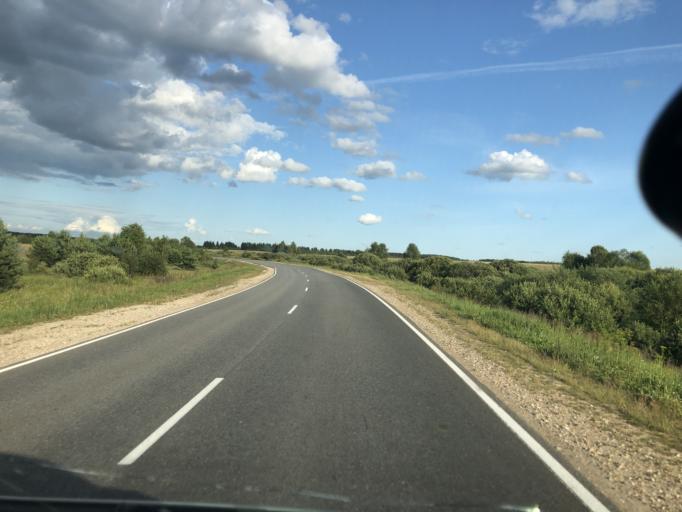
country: RU
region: Kaluga
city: Yukhnov
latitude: 54.7012
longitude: 35.2722
